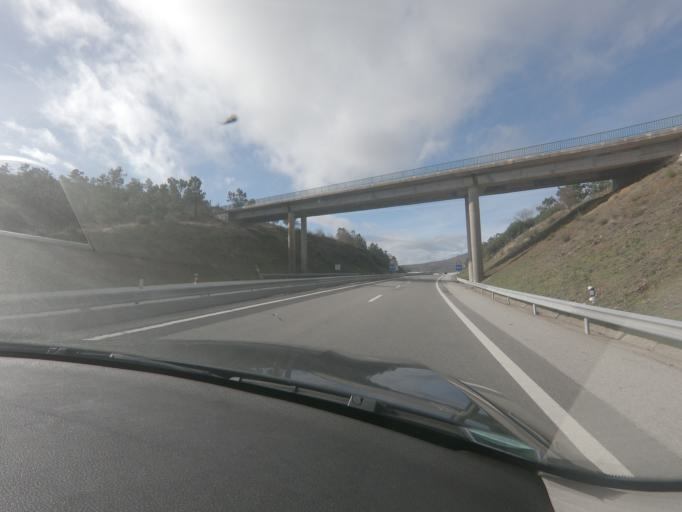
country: PT
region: Viseu
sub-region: Lamego
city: Lamego
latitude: 41.0495
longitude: -7.8529
